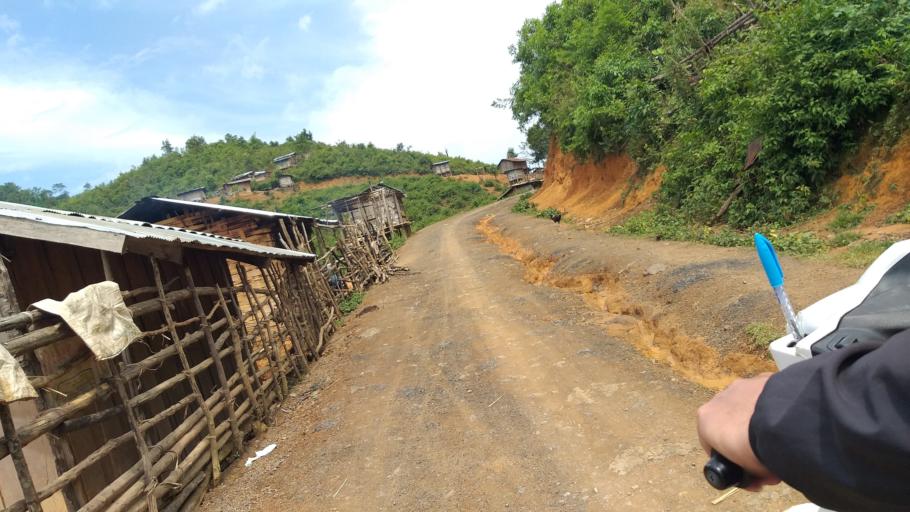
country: VN
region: Huyen Dien Bien
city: Dien Bien Phu
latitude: 21.4136
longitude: 102.6844
